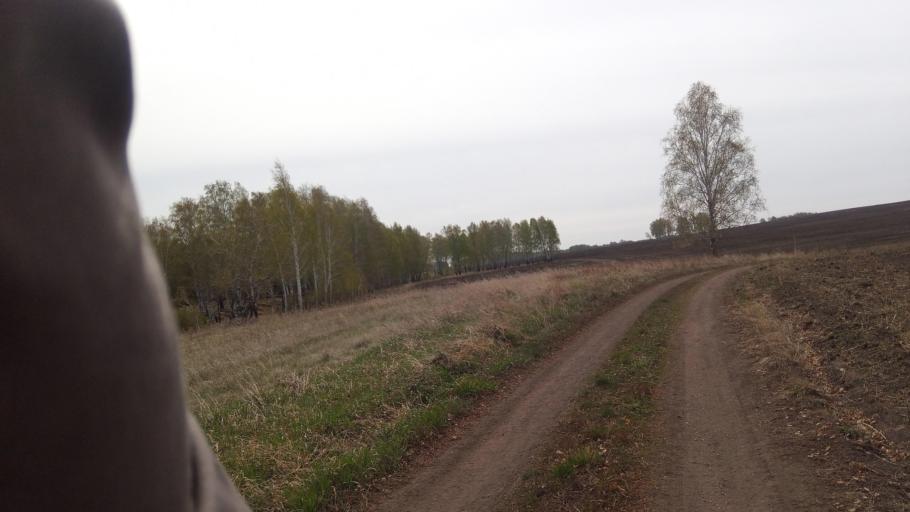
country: RU
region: Chelyabinsk
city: Timiryazevskiy
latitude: 55.0223
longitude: 60.8517
